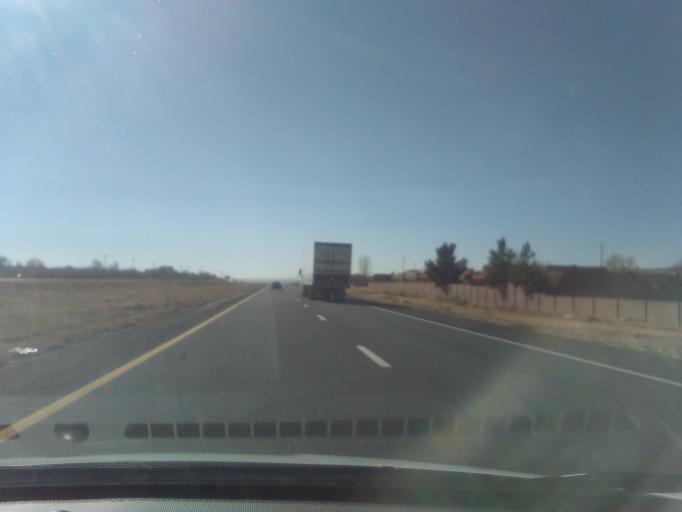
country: US
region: New Mexico
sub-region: Valencia County
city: Los Lunas
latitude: 34.8067
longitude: -106.7647
